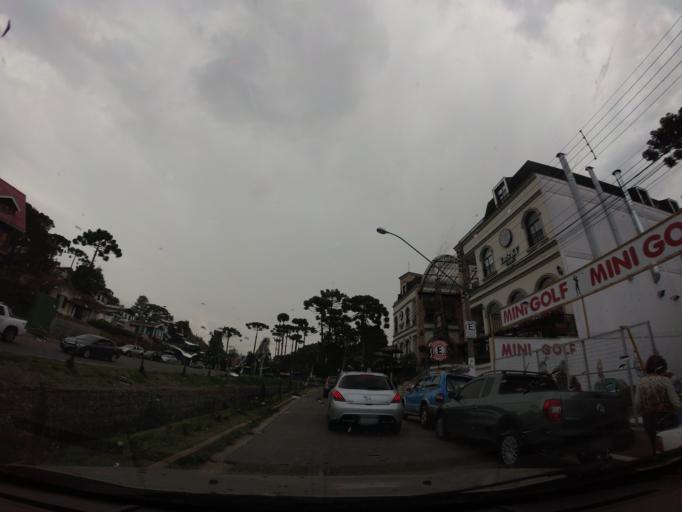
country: BR
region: Sao Paulo
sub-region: Campos Do Jordao
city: Campos do Jordao
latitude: -22.7199
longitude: -45.5662
